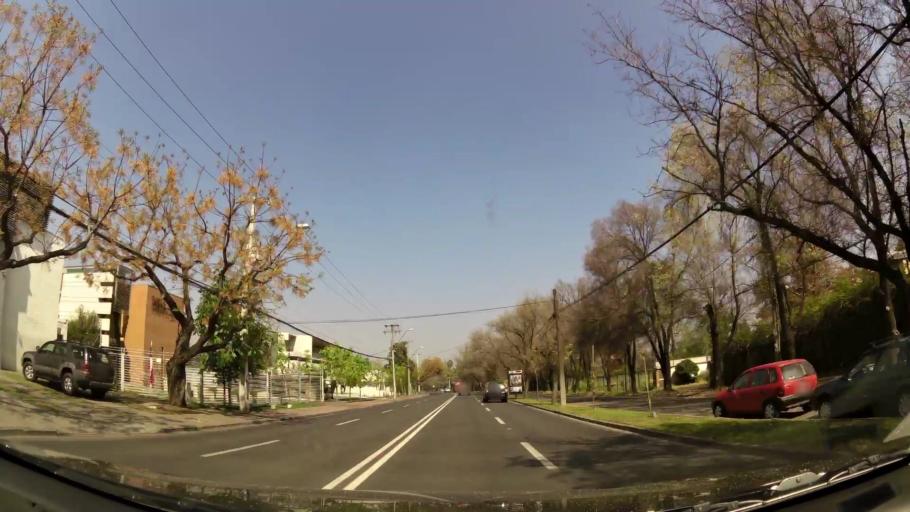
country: CL
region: Santiago Metropolitan
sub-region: Provincia de Santiago
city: Villa Presidente Frei, Nunoa, Santiago, Chile
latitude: -33.3916
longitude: -70.5802
